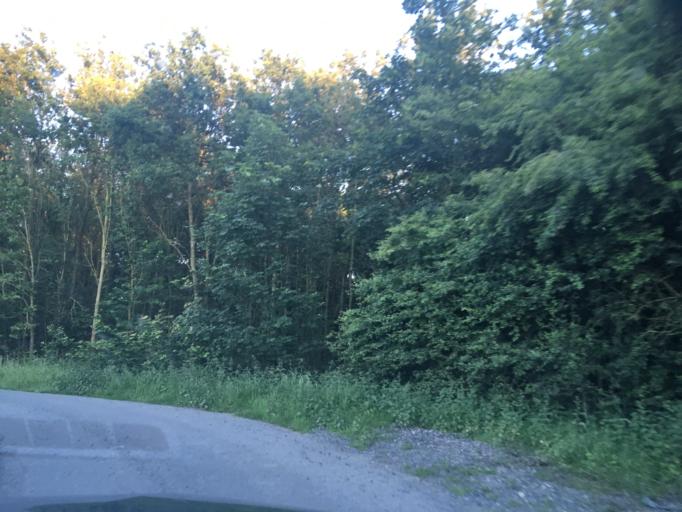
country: BE
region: Flanders
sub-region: Provincie West-Vlaanderen
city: Ieper
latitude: 50.8193
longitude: 2.9064
